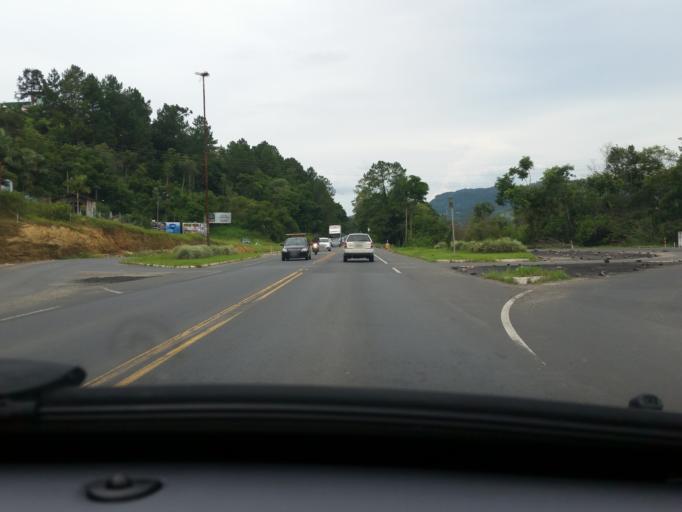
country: BR
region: Santa Catarina
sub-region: Rio Do Sul
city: Rio do Sul
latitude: -27.2573
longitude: -49.7131
